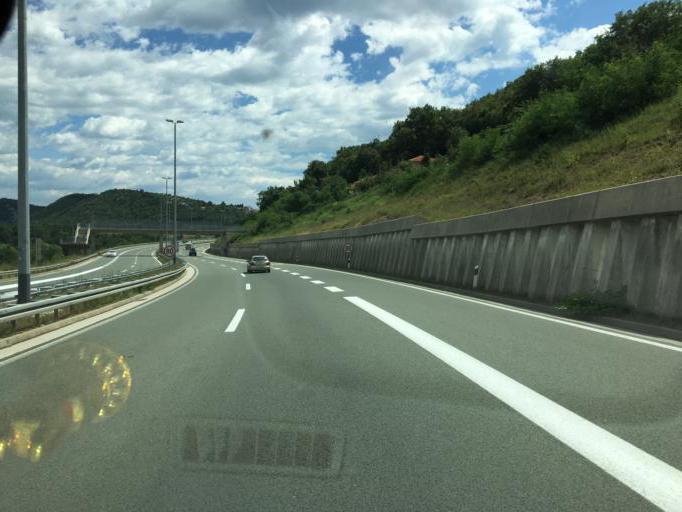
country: HR
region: Primorsko-Goranska
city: Cavle
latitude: 45.3349
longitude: 14.4727
